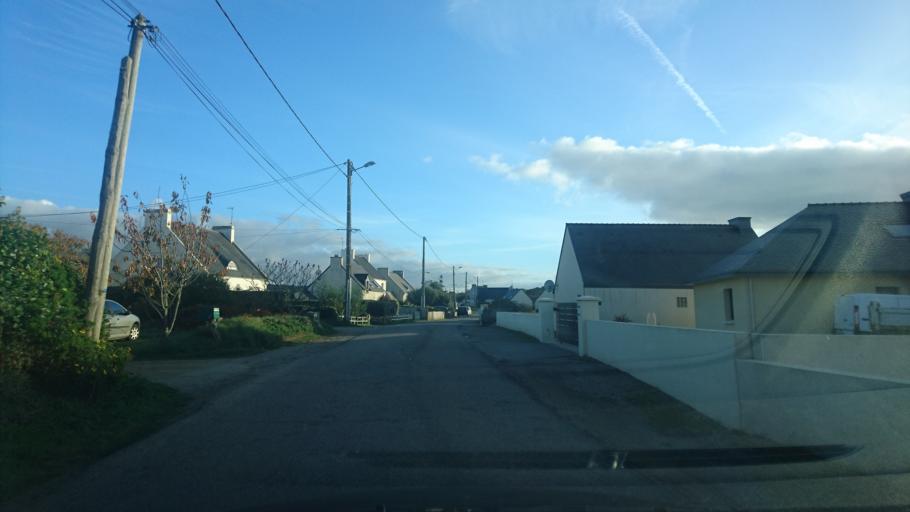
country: FR
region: Brittany
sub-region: Departement du Finistere
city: Lampaul-Plouarzel
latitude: 48.4410
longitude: -4.7674
